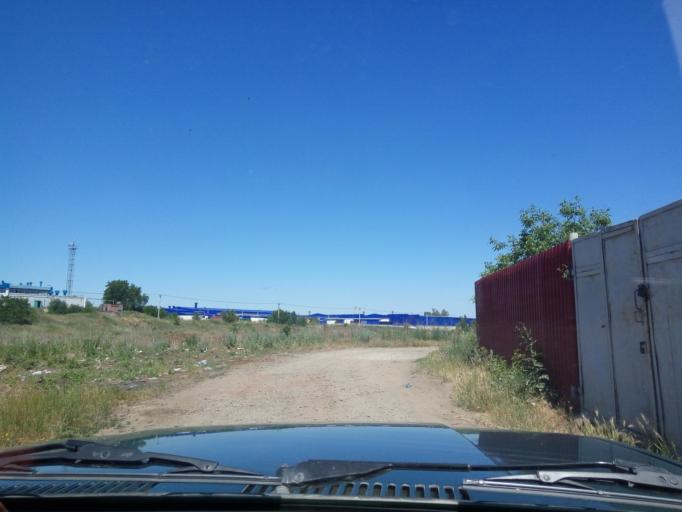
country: RU
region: Rostov
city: Bataysk
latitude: 47.0807
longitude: 39.7477
